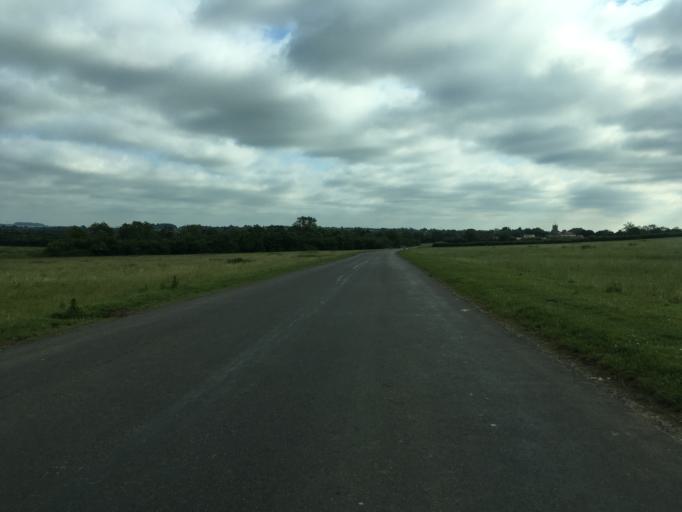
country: GB
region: England
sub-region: South Gloucestershire
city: Chipping Sodbury
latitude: 51.5477
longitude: -2.3799
